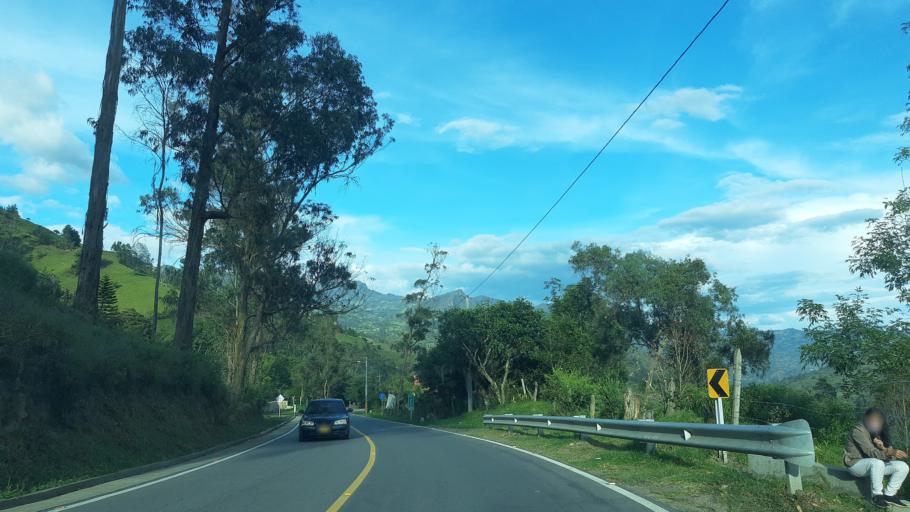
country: CO
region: Cundinamarca
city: Macheta
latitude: 5.0769
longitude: -73.5990
